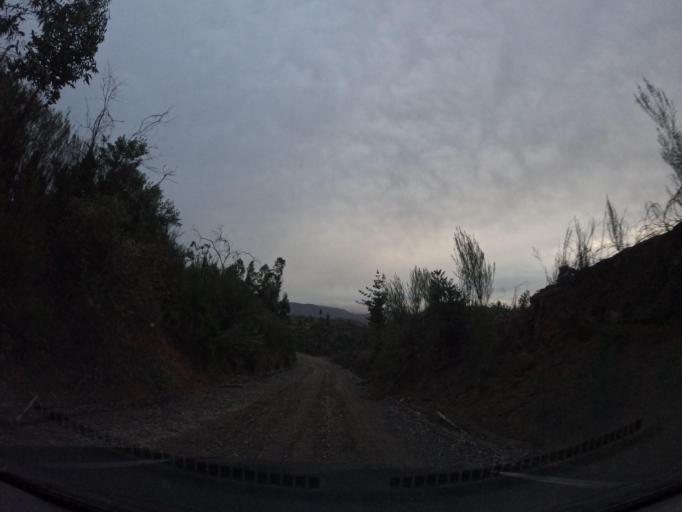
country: CL
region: Biobio
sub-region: Provincia de Concepcion
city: Chiguayante
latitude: -37.0095
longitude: -72.8944
